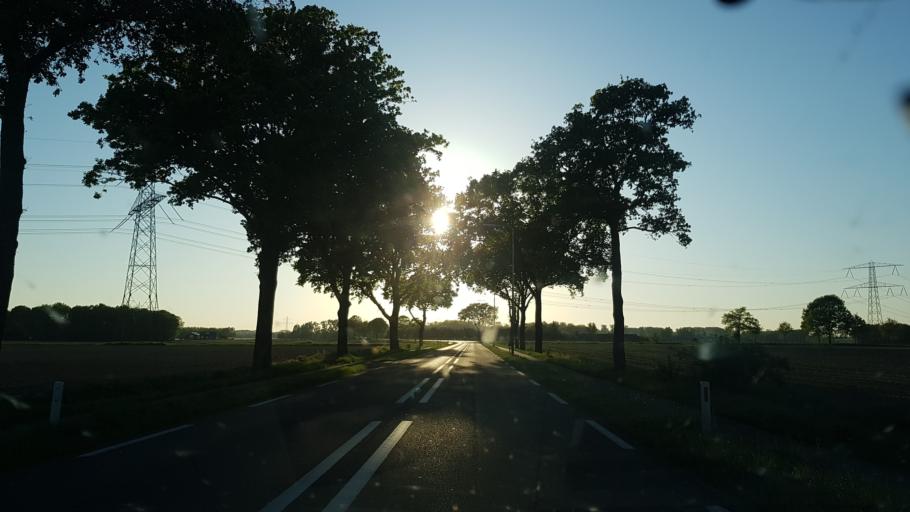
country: NL
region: Limburg
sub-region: Gemeente Leudal
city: Kelpen-Oler
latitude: 51.2271
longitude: 5.8546
